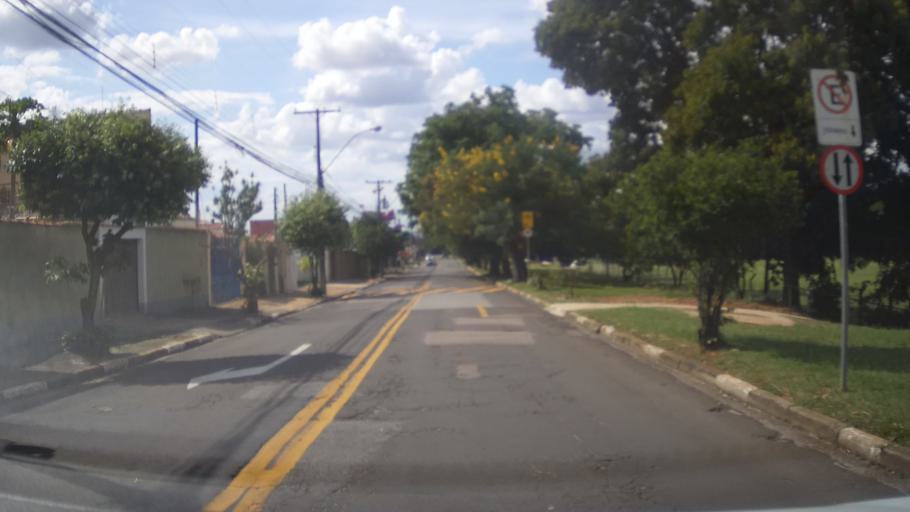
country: BR
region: Sao Paulo
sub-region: Campinas
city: Campinas
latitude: -22.8871
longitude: -47.1050
